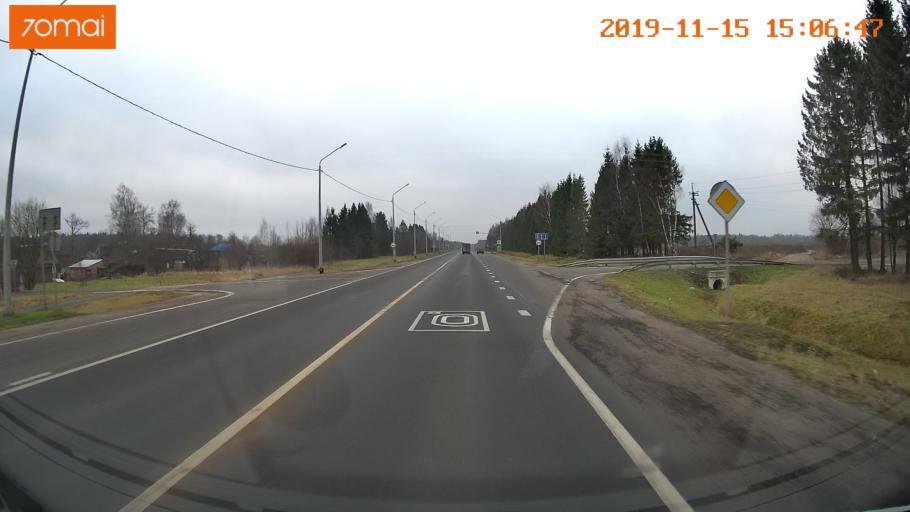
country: RU
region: Jaroslavl
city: Prechistoye
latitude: 58.3897
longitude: 40.3056
